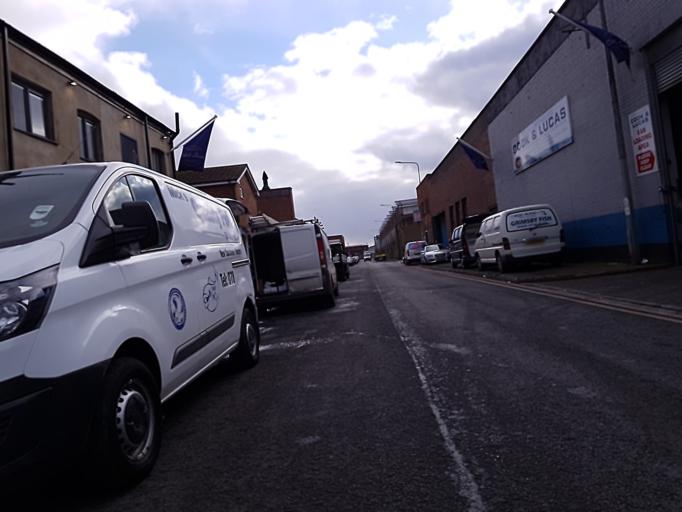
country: GB
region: England
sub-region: North East Lincolnshire
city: Grimsby
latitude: 53.5756
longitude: -0.0686
